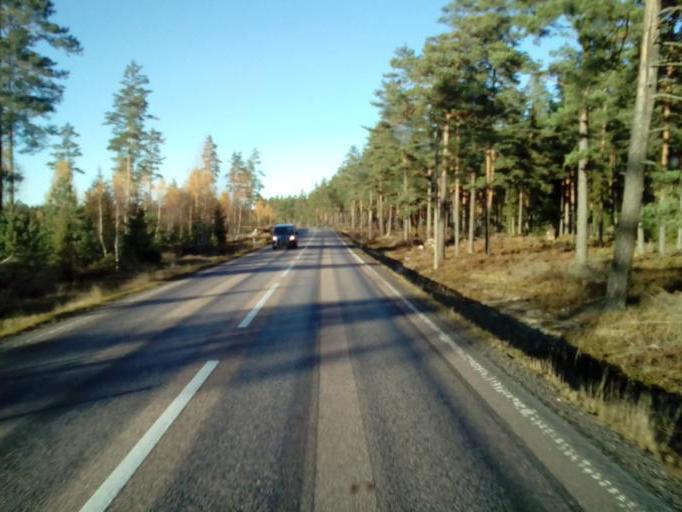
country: SE
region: OErebro
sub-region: Hallsbergs Kommun
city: Palsboda
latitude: 58.8483
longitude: 15.4044
